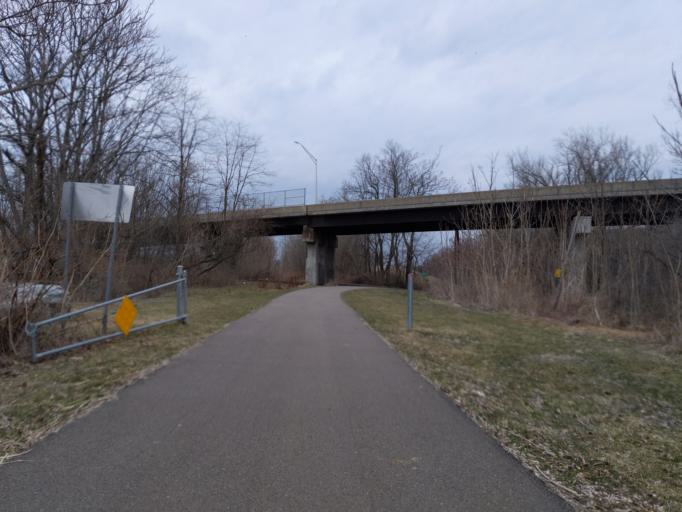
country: US
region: New York
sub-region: Chemung County
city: Elmira
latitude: 42.0899
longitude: -76.7837
